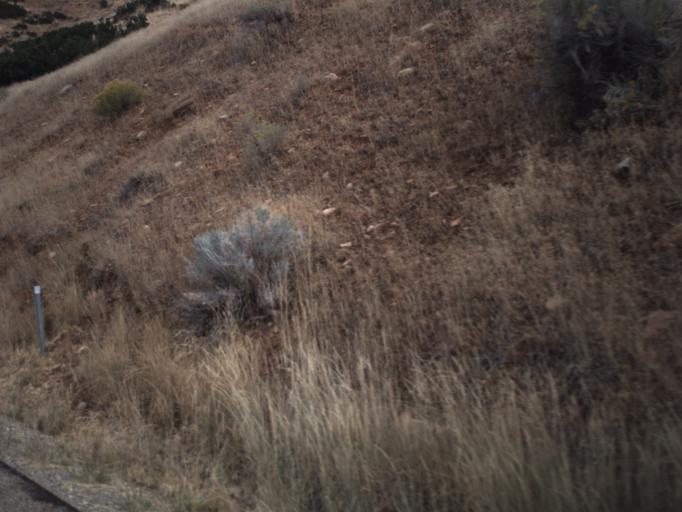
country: US
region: Utah
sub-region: Morgan County
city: Morgan
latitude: 40.9346
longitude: -111.6293
